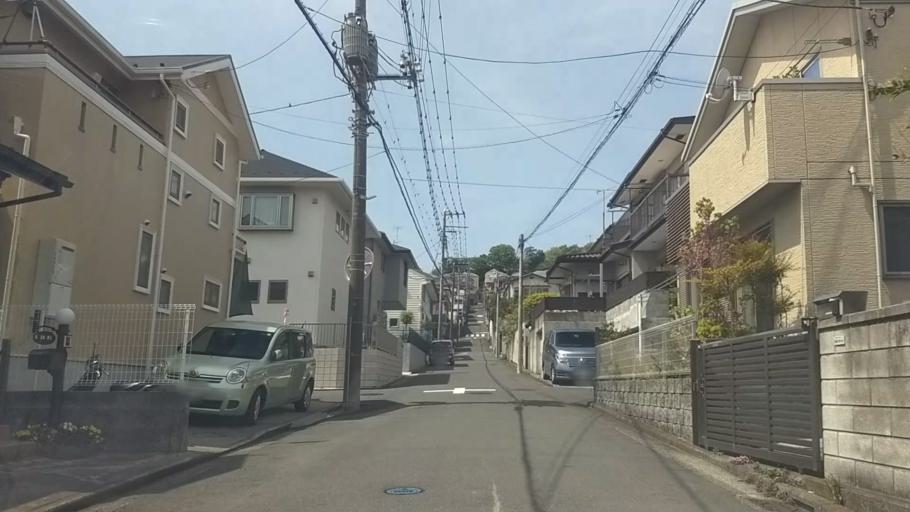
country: JP
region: Kanagawa
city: Yokohama
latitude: 35.3917
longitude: 139.5929
